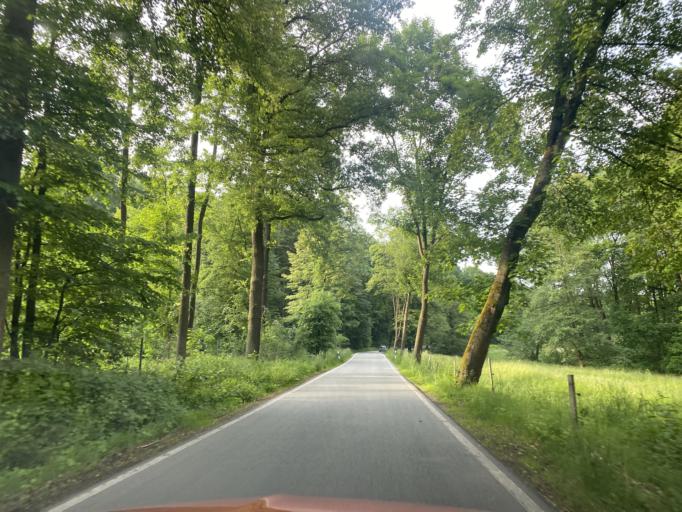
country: DE
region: Saxony
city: Bernstadt
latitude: 51.0347
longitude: 14.8018
